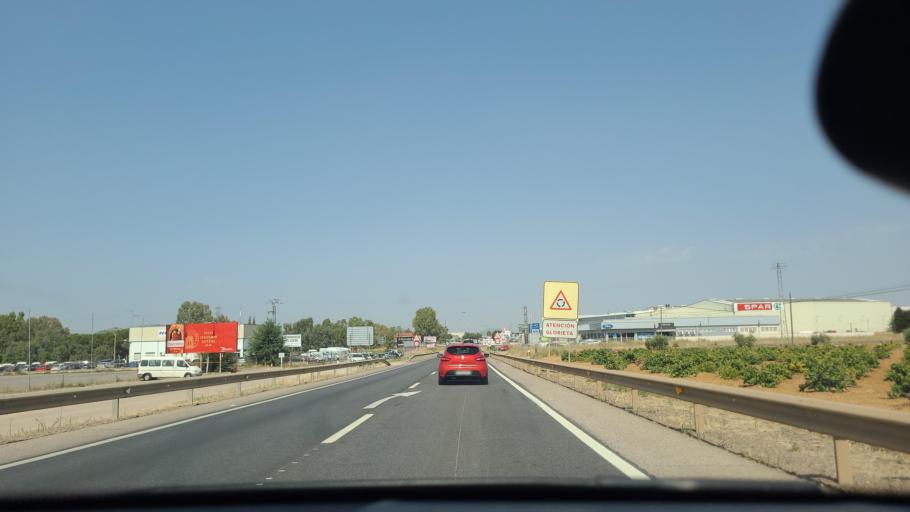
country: ES
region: Extremadura
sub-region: Provincia de Badajoz
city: Puebla de Sancho Perez
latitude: 38.4129
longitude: -6.3958
